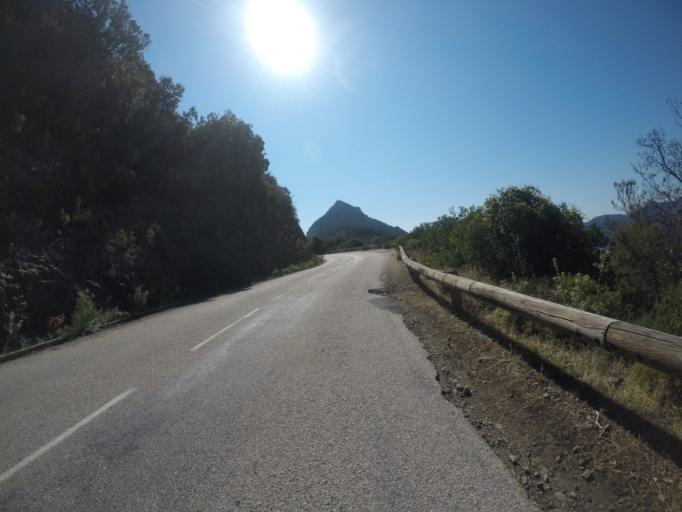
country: FR
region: Corsica
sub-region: Departement de la Corse-du-Sud
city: Cargese
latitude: 42.3288
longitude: 8.6363
